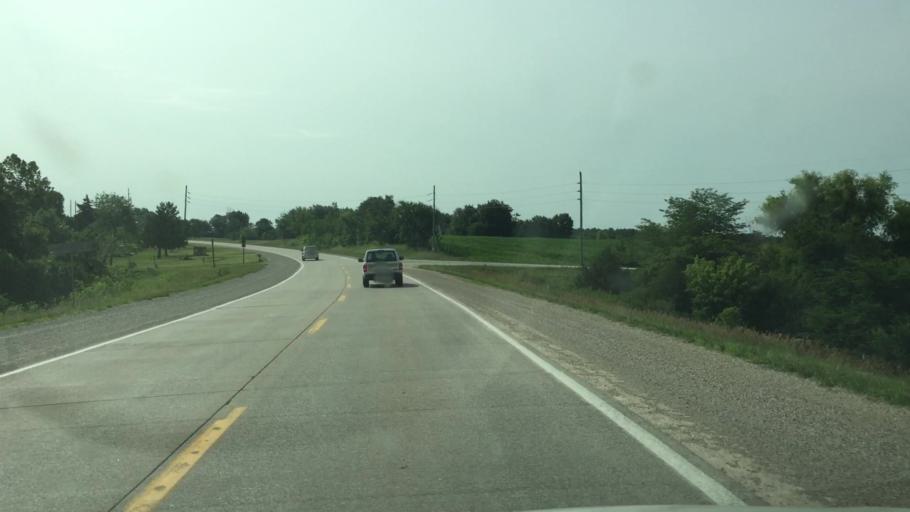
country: US
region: Illinois
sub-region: Hancock County
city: Nauvoo
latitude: 40.6342
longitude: -91.5160
